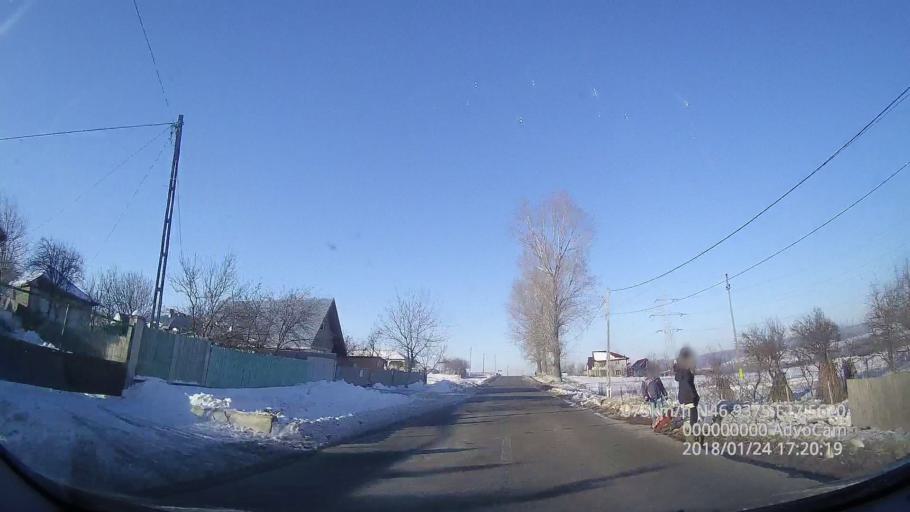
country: RO
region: Iasi
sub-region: Comuna Scanteia
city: Scanteia
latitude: 46.9382
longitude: 27.5618
